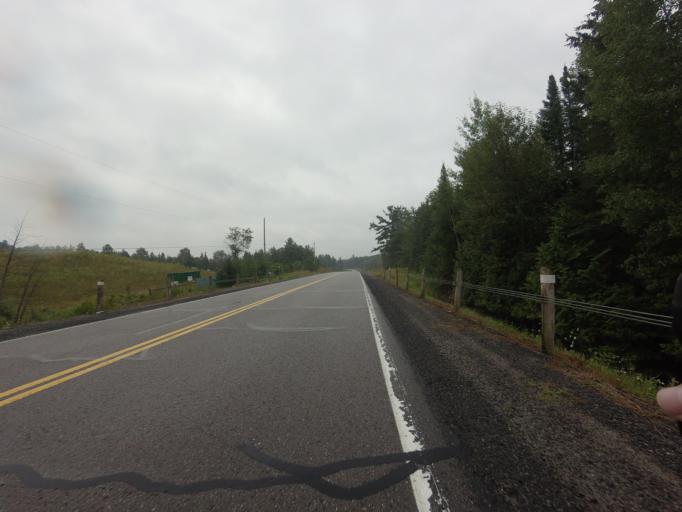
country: CA
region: Ontario
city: Perth
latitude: 45.0874
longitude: -76.4220
